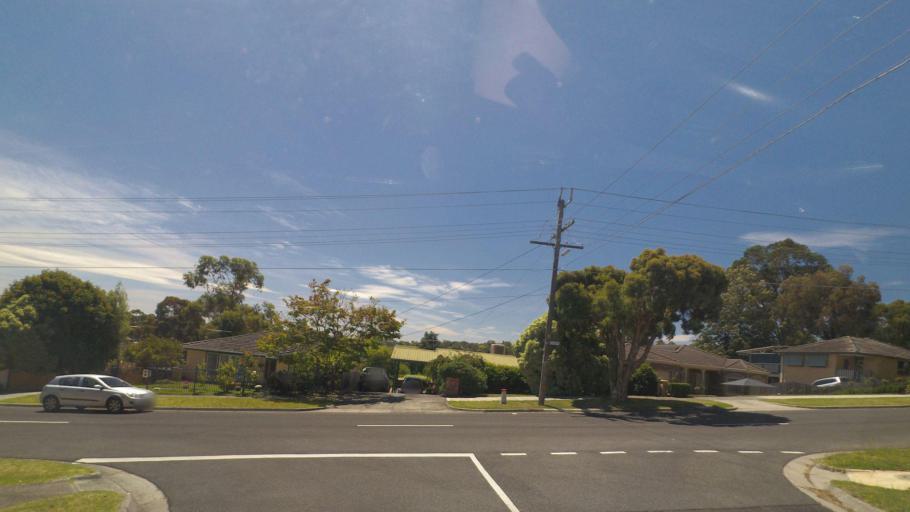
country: AU
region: Victoria
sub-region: Maroondah
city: Croydon North
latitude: -37.7792
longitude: 145.3189
